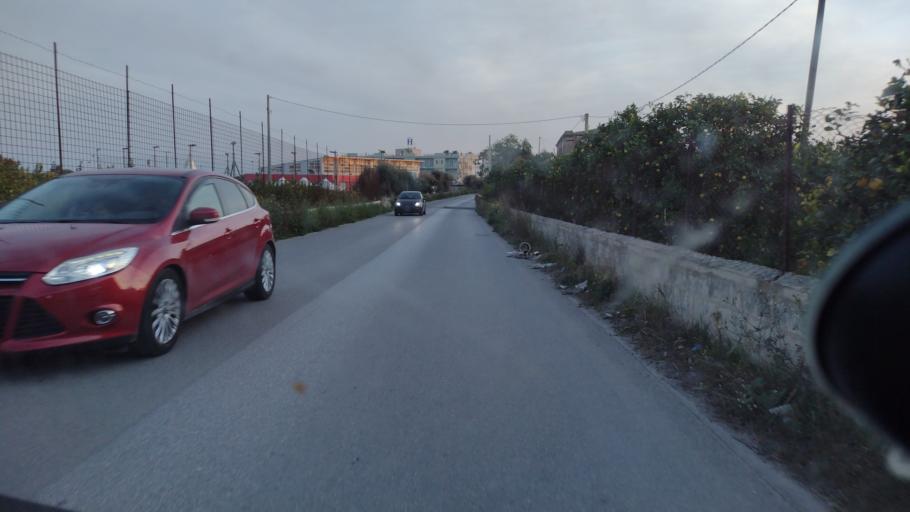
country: IT
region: Sicily
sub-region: Provincia di Siracusa
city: Avola
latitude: 36.8970
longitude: 15.1341
